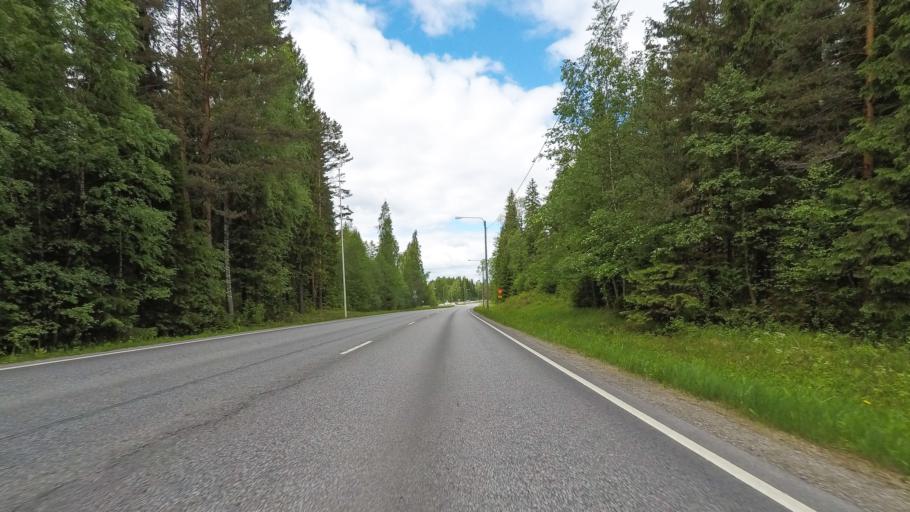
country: FI
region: Central Finland
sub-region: Jyvaeskylae
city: Toivakka
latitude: 62.2475
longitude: 26.1759
